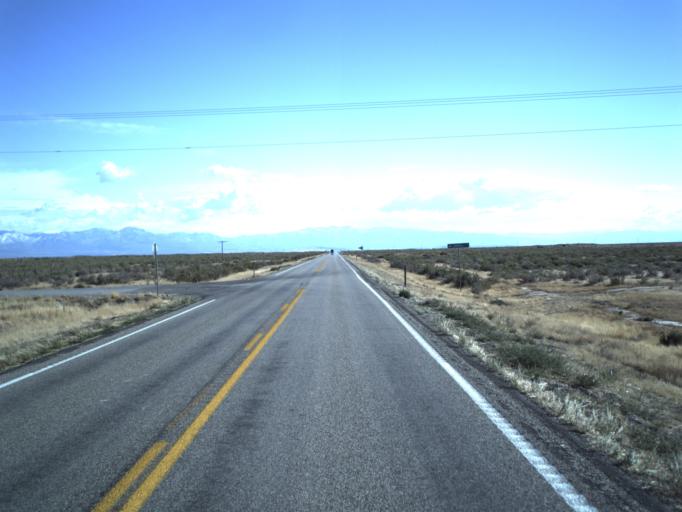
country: US
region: Utah
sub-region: Millard County
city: Delta
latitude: 39.3210
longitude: -112.4822
